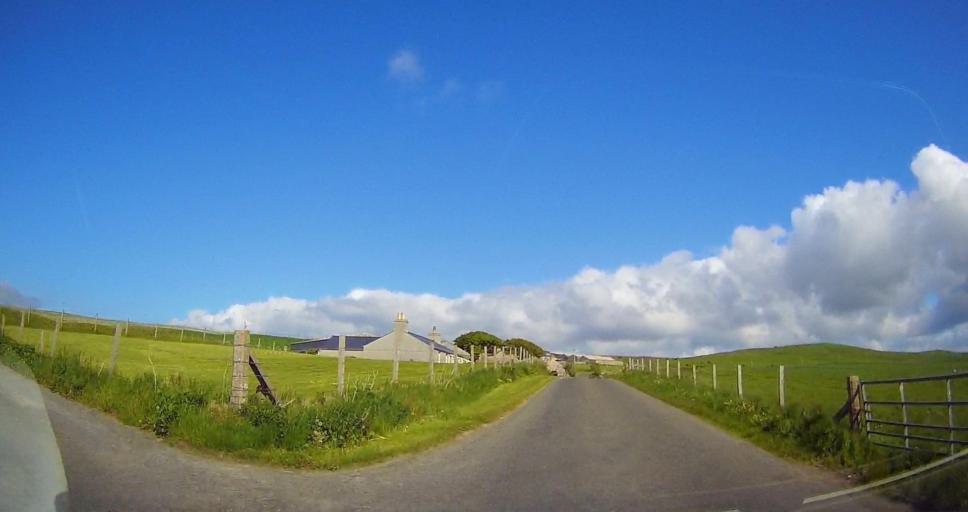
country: GB
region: Scotland
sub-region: Orkney Islands
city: Stromness
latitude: 58.9832
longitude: -3.1441
